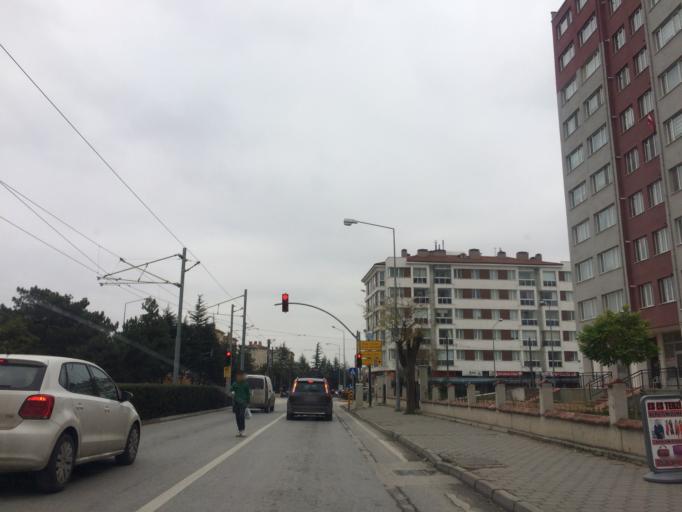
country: TR
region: Eskisehir
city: Eskisehir
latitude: 39.7897
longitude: 30.4888
